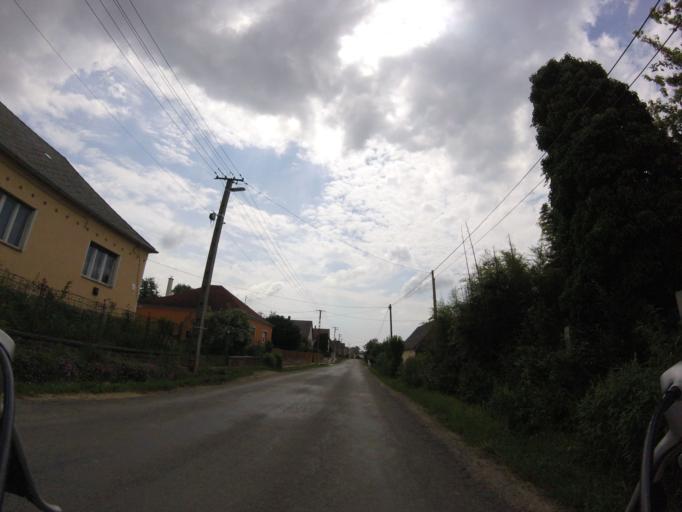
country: HU
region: Baranya
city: Kozarmisleny
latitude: 46.0626
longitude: 18.3736
